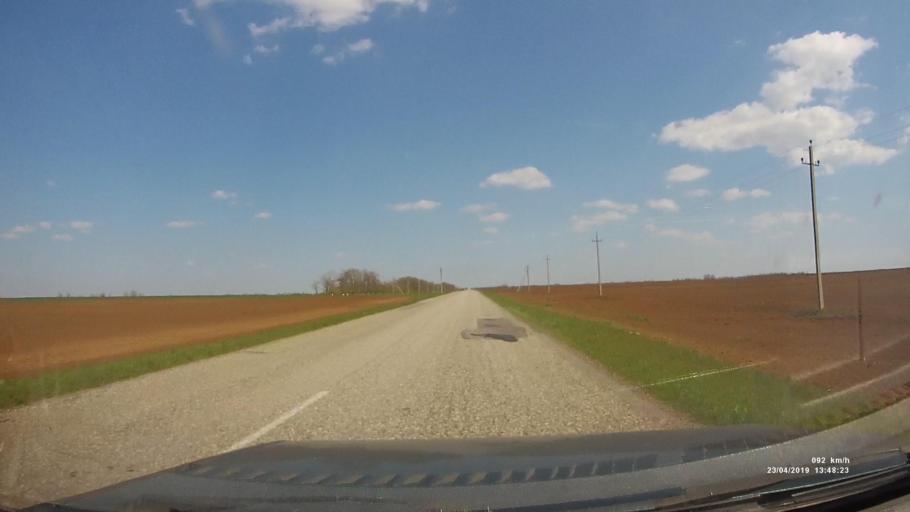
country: RU
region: Kalmykiya
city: Yashalta
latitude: 46.5991
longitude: 42.8726
